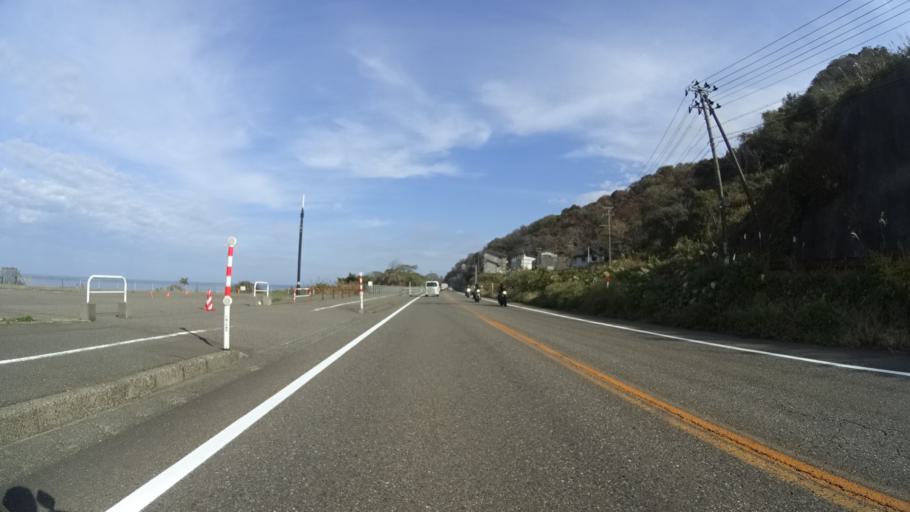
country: JP
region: Niigata
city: Joetsu
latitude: 37.1669
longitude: 138.1869
